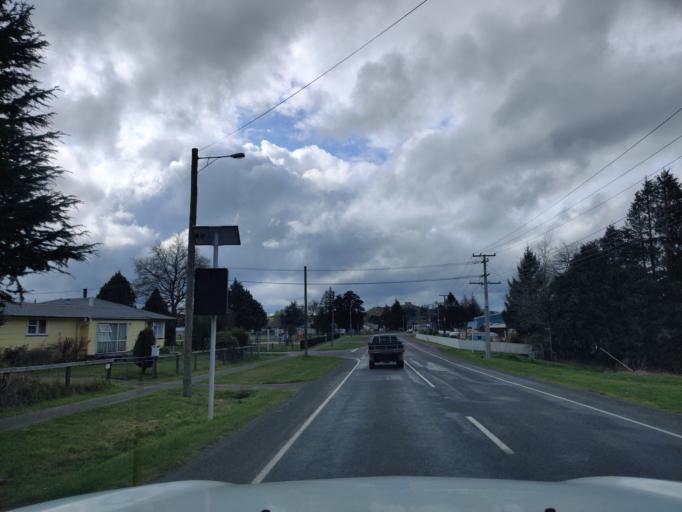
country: NZ
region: Manawatu-Wanganui
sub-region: Ruapehu District
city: Waiouru
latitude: -39.4315
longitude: 175.2824
